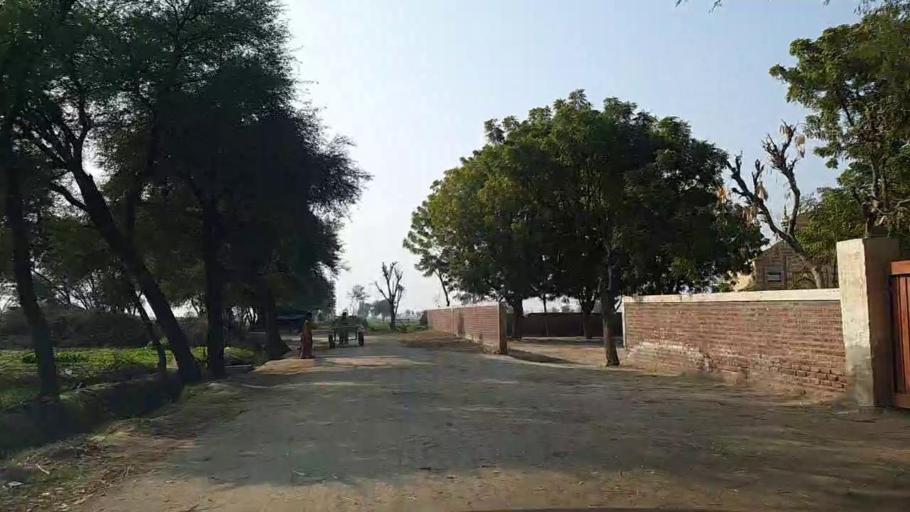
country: PK
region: Sindh
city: Daur
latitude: 26.3997
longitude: 68.4167
